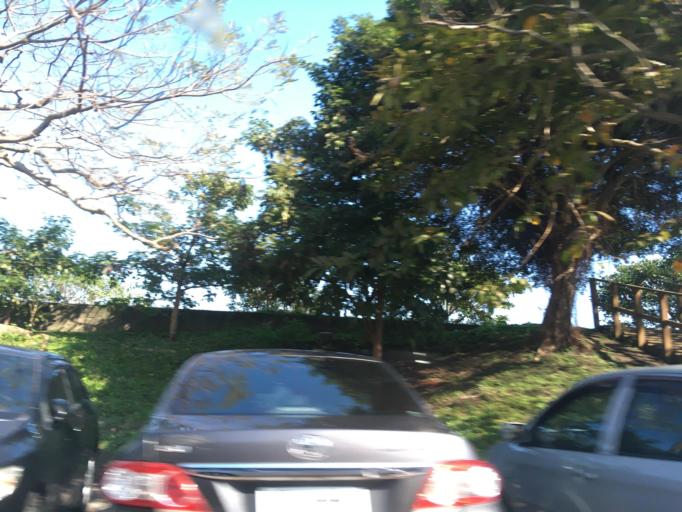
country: TW
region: Taiwan
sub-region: Yilan
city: Yilan
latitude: 24.7633
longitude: 121.7590
